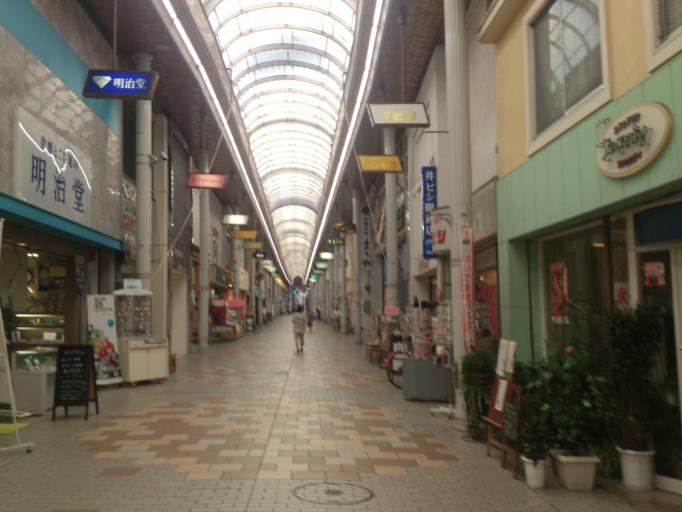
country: JP
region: Yamaguchi
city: Yamaguchi-shi
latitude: 34.1749
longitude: 131.4756
